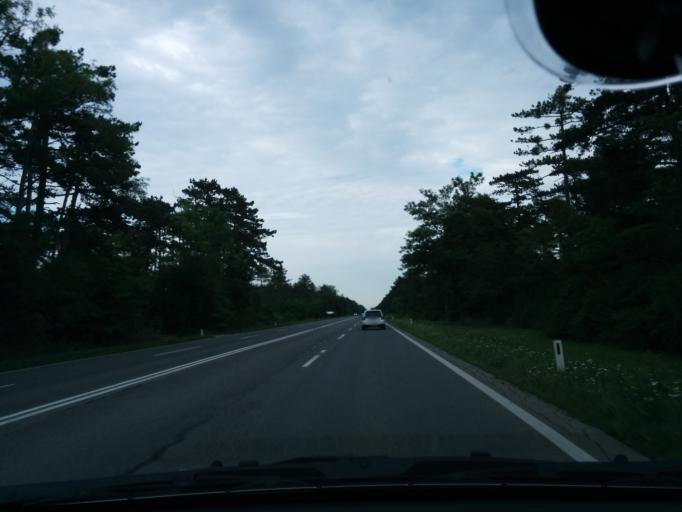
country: AT
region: Lower Austria
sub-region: Politischer Bezirk Neunkirchen
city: Breitenau
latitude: 47.7645
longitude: 16.1605
